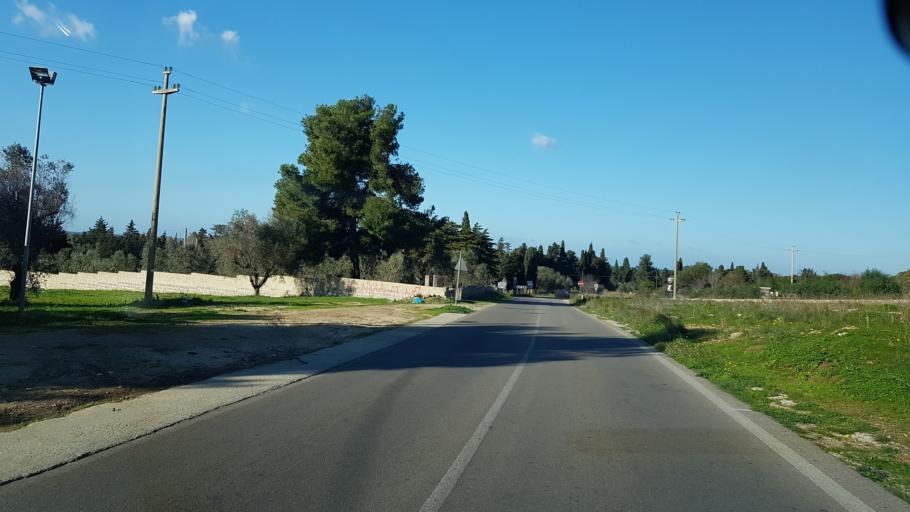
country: IT
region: Apulia
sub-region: Provincia di Lecce
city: Sannicola
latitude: 40.0968
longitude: 18.0225
